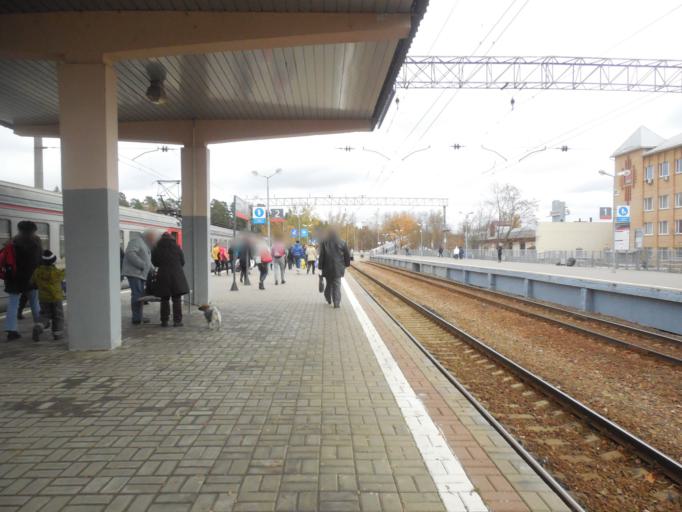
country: RU
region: Moskovskaya
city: Zvenigorod
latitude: 55.7002
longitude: 36.8795
